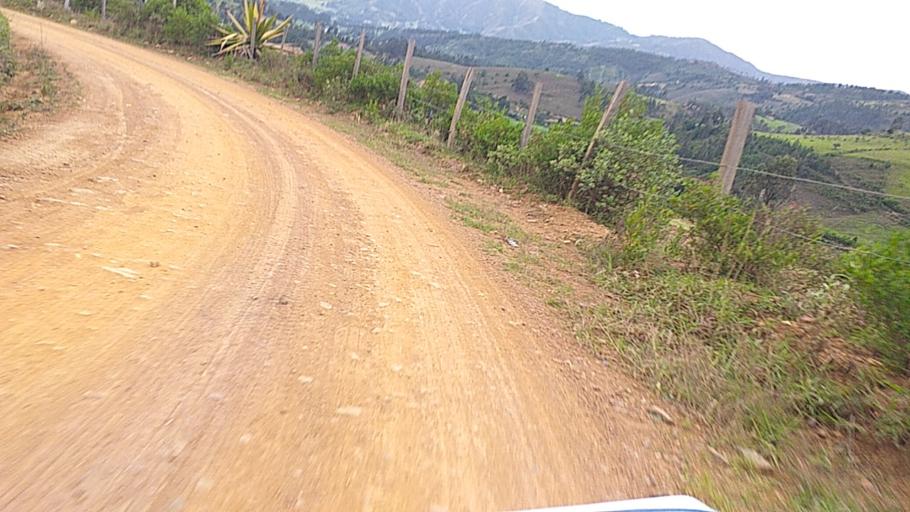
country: CO
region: Boyaca
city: Floresta
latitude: 5.8786
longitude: -72.9137
